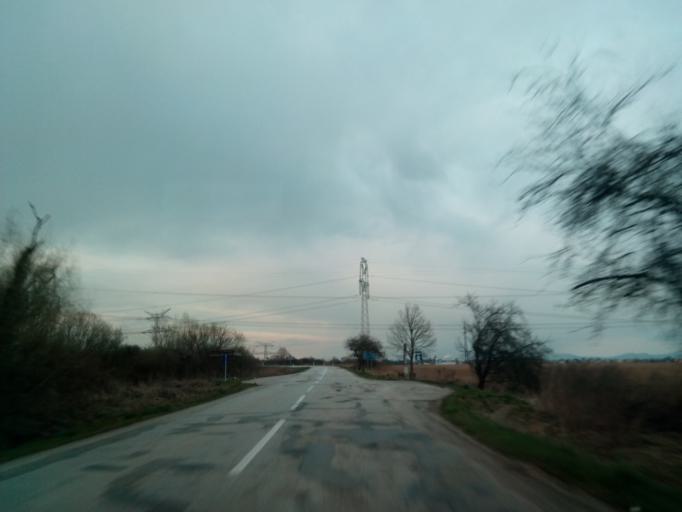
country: SK
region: Kosicky
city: Moldava nad Bodvou
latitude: 48.5971
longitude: 21.0418
